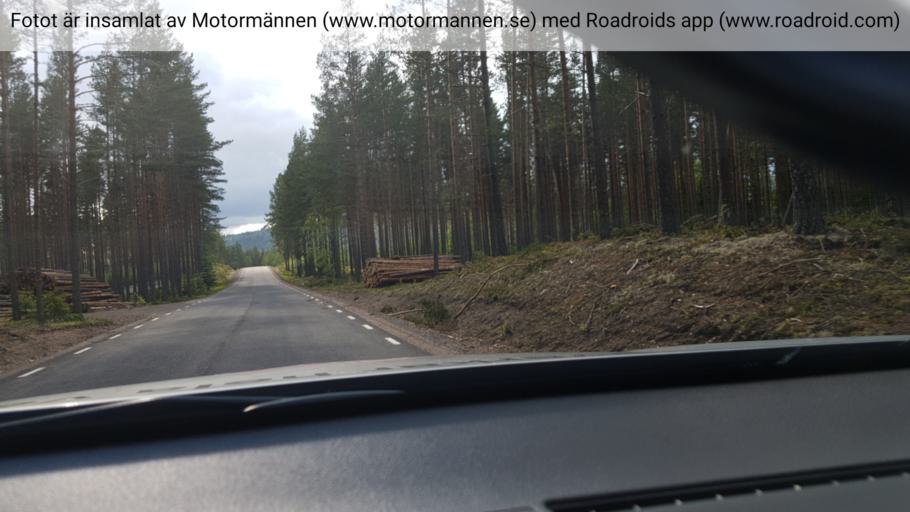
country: SE
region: Vaermland
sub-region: Hagfors Kommun
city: Ekshaerad
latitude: 60.2996
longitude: 13.4371
